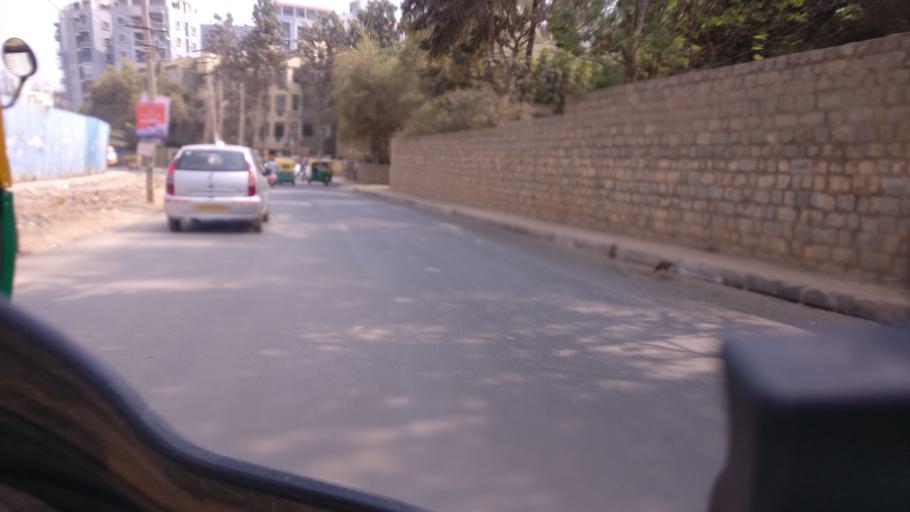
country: IN
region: Karnataka
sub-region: Bangalore Urban
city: Bangalore
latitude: 12.9097
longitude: 77.6767
